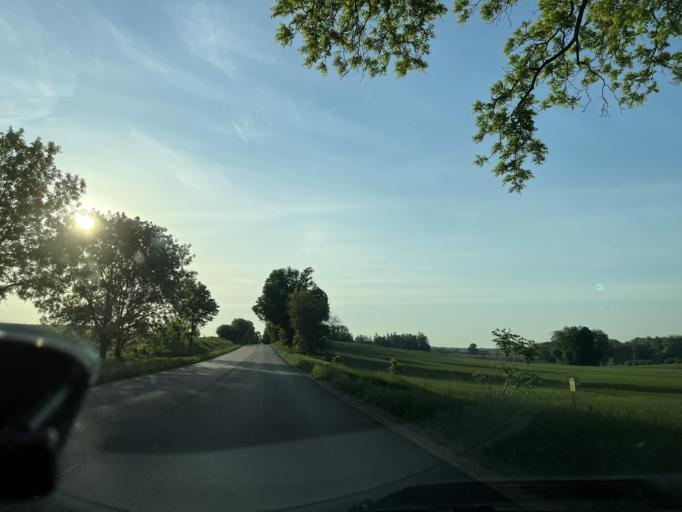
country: US
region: Michigan
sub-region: Barry County
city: Middleville
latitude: 42.7111
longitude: -85.4368
